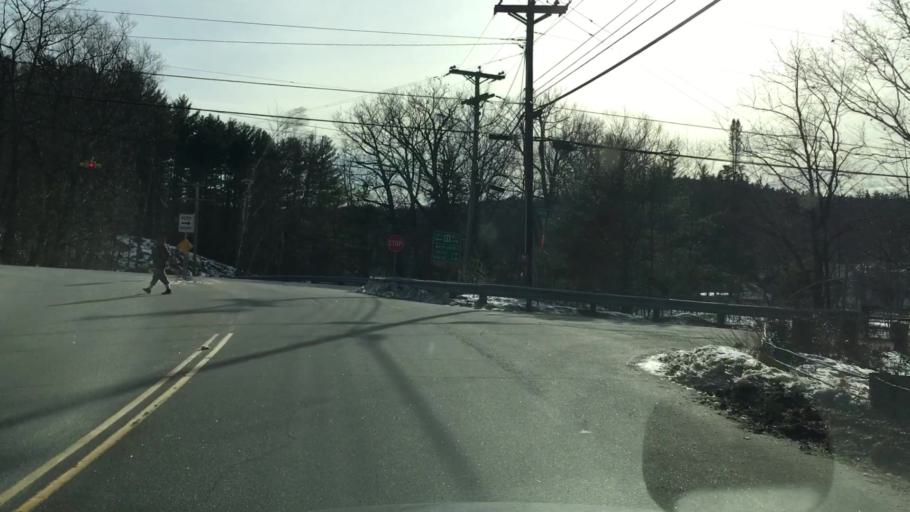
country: US
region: New Hampshire
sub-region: Sullivan County
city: Sunapee
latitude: 43.4322
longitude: -72.0666
